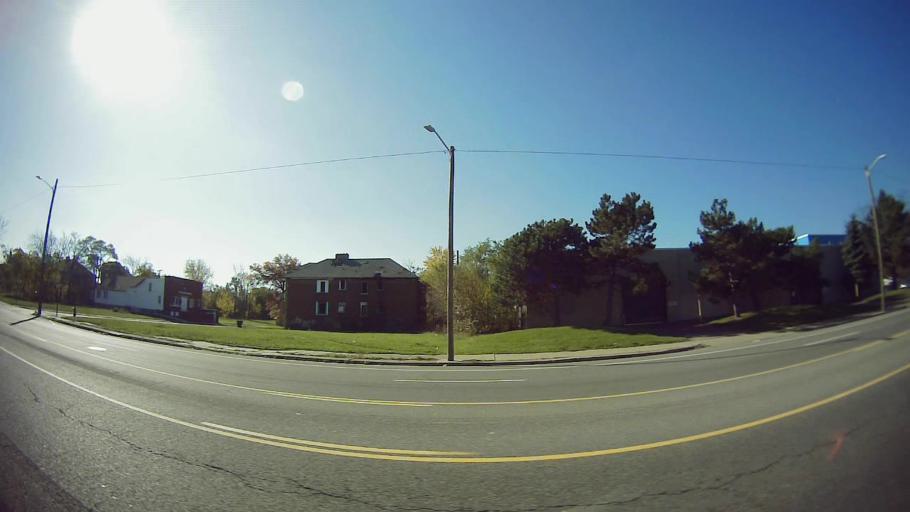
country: US
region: Michigan
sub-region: Wayne County
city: Highland Park
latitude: 42.3918
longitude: -83.1211
